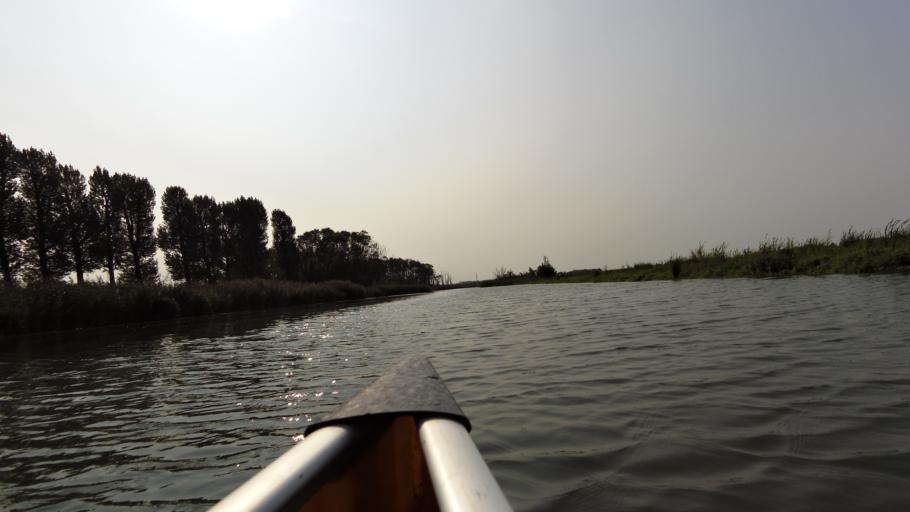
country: NL
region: South Holland
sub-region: Gemeente Sliedrecht
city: Sliedrecht
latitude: 51.7739
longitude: 4.8081
